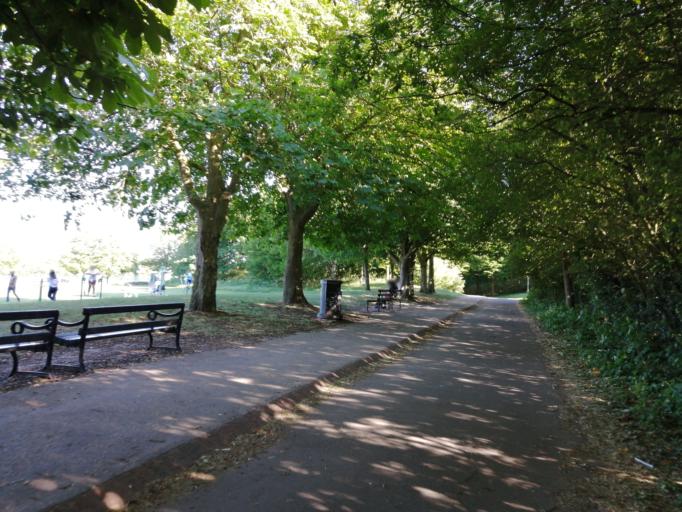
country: GB
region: England
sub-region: Peterborough
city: Marholm
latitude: 52.5964
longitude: -0.2818
